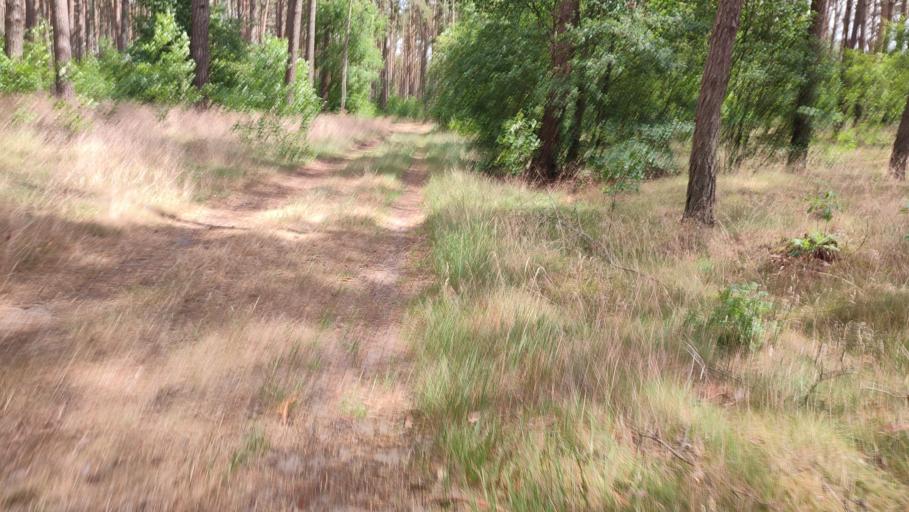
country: DE
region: Lower Saxony
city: Hitzacker
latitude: 53.2123
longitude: 11.0707
